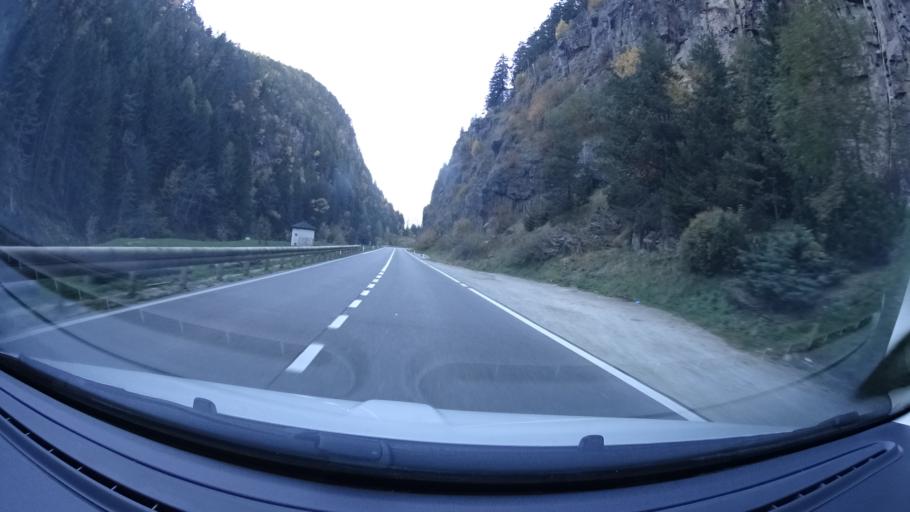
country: IT
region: Trentino-Alto Adige
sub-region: Bolzano
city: Ortisei
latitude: 46.5772
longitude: 11.6432
